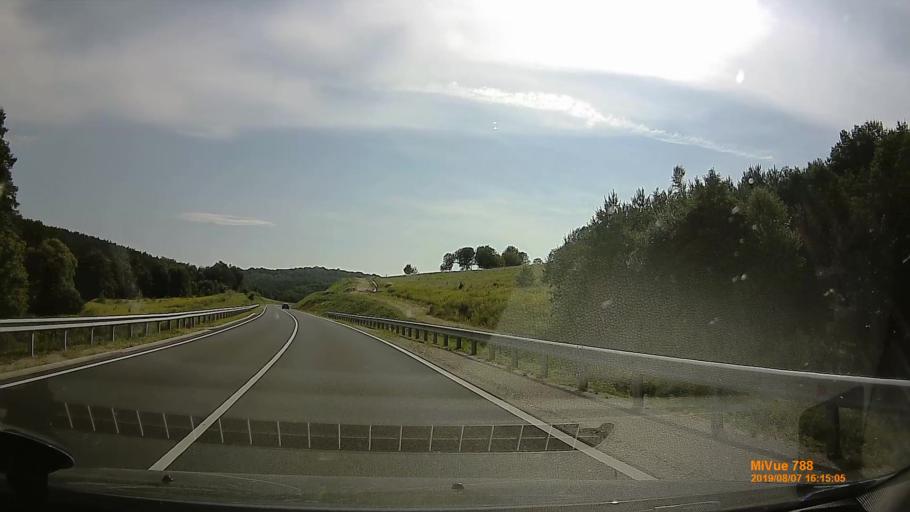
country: HU
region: Zala
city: Zalalovo
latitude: 46.8291
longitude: 16.6033
